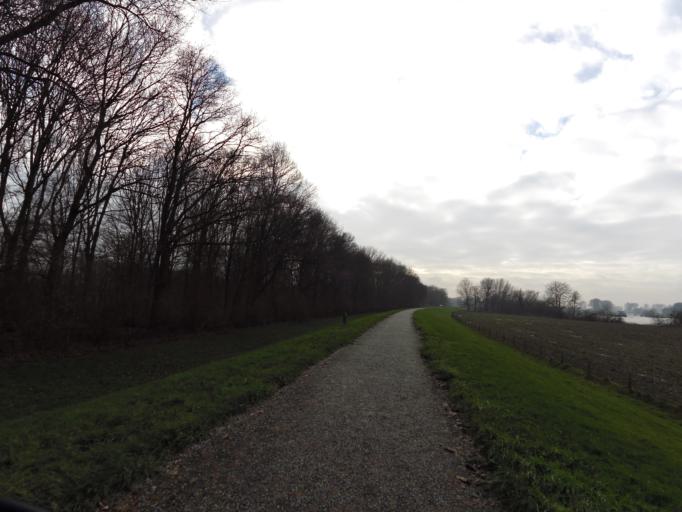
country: NL
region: Gelderland
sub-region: Gemeente Doesburg
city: Doesburg
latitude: 51.9980
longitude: 6.1134
